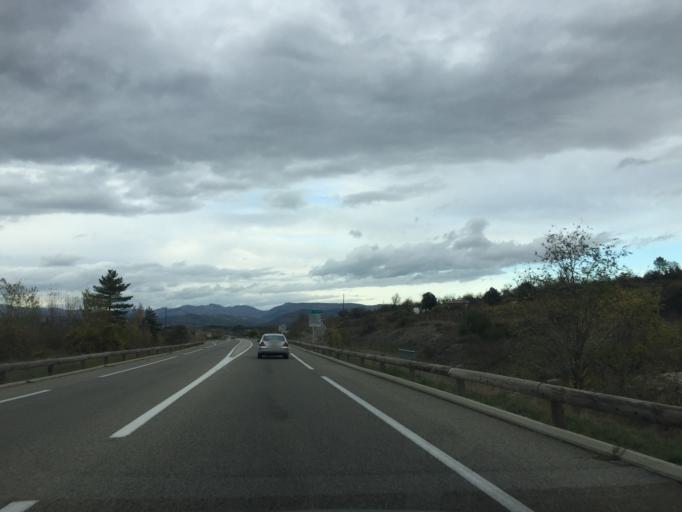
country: FR
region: Rhone-Alpes
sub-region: Departement de l'Ardeche
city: Lachapelle-sous-Aubenas
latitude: 44.5669
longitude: 4.3730
